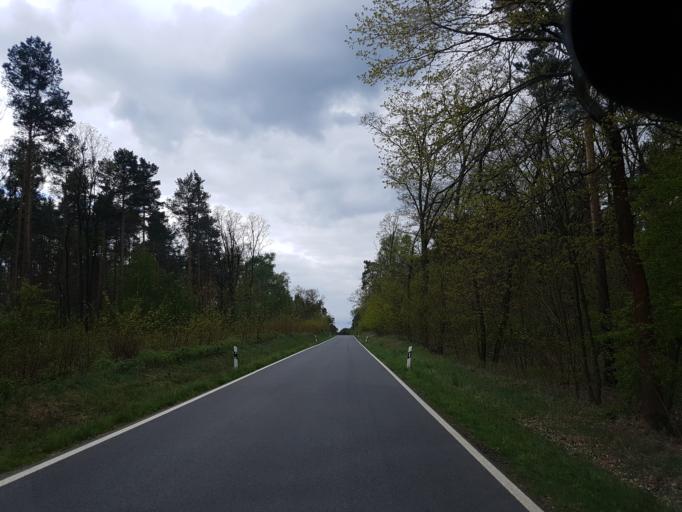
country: DE
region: Brandenburg
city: Altdobern
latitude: 51.6492
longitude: 13.9849
